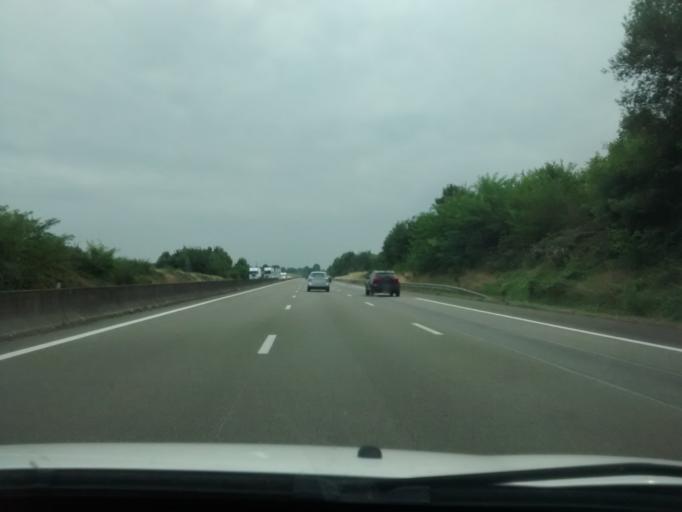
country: FR
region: Pays de la Loire
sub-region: Departement de la Sarthe
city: Neuville-sur-Sarthe
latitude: 48.0586
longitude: 0.2114
